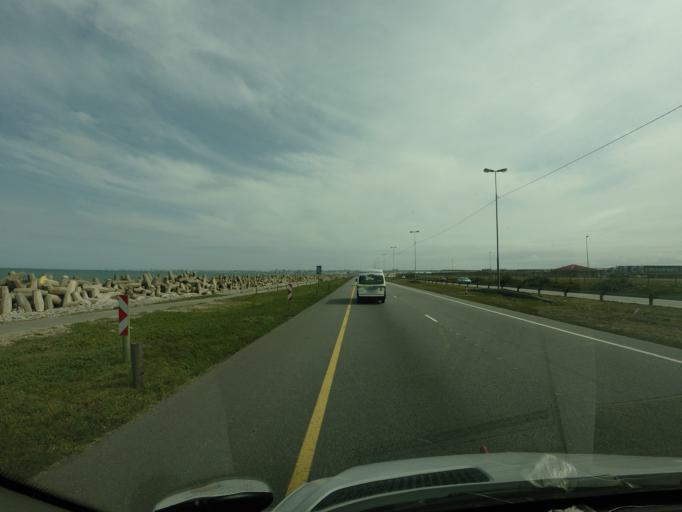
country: ZA
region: Eastern Cape
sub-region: Nelson Mandela Bay Metropolitan Municipality
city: Port Elizabeth
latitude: -33.9072
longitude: 25.6174
